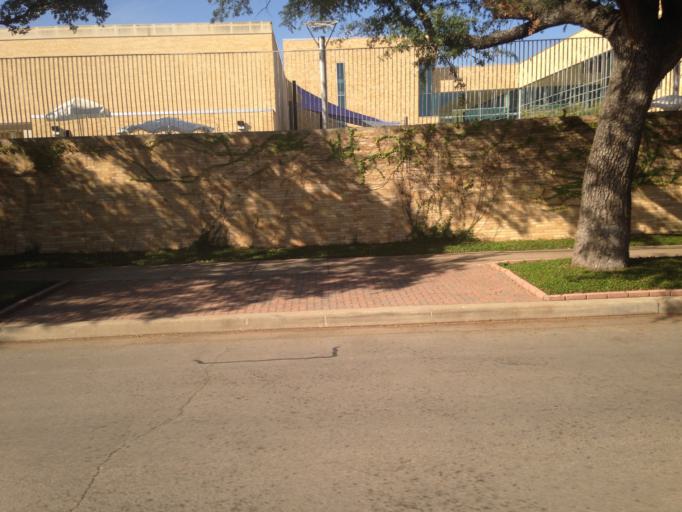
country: US
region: Texas
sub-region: Tarrant County
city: Fort Worth
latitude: 32.7071
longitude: -97.3640
